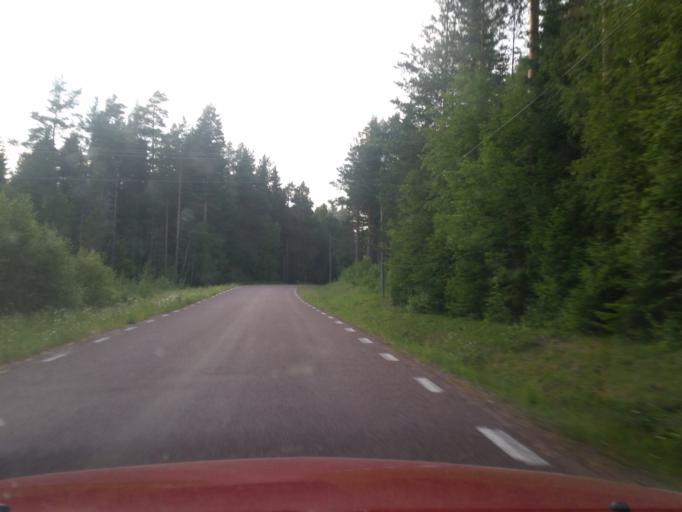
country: SE
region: Dalarna
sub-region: Gagnefs Kommun
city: Gagnef
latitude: 60.6750
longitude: 15.1722
